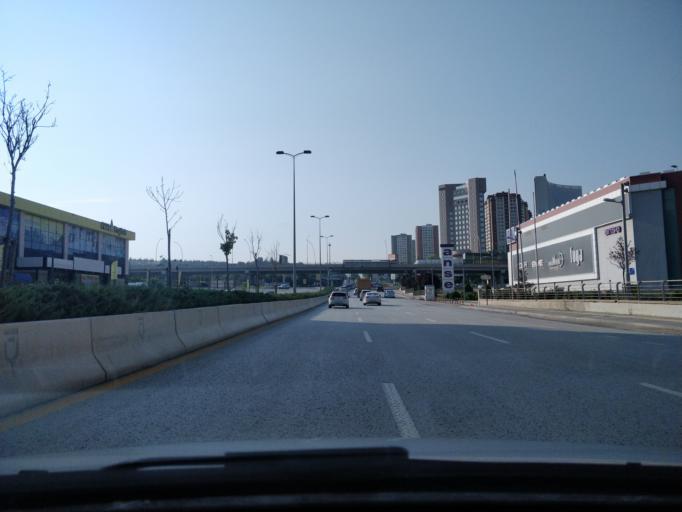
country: TR
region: Ankara
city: Etimesgut
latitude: 39.8964
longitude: 32.6775
